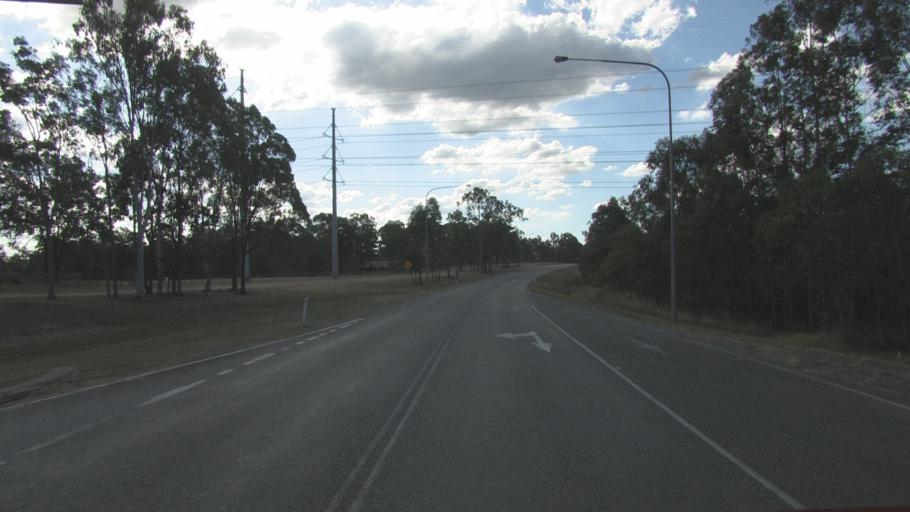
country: AU
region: Queensland
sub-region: Logan
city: Park Ridge South
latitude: -27.7299
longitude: 152.9841
